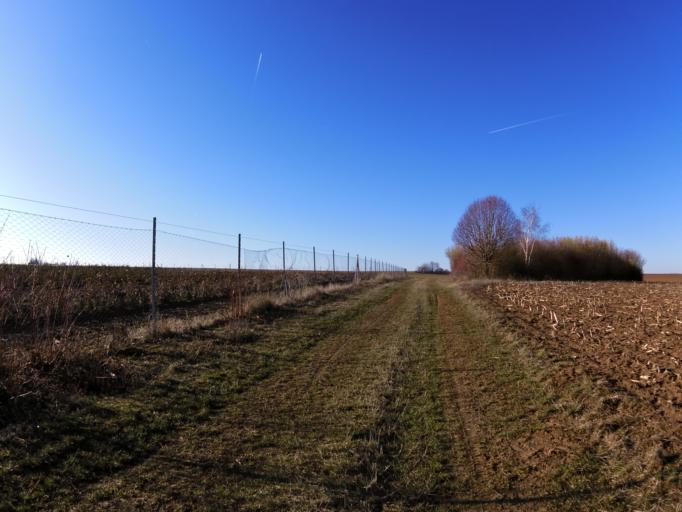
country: DE
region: Bavaria
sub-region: Regierungsbezirk Unterfranken
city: Estenfeld
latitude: 49.8429
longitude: 9.9952
